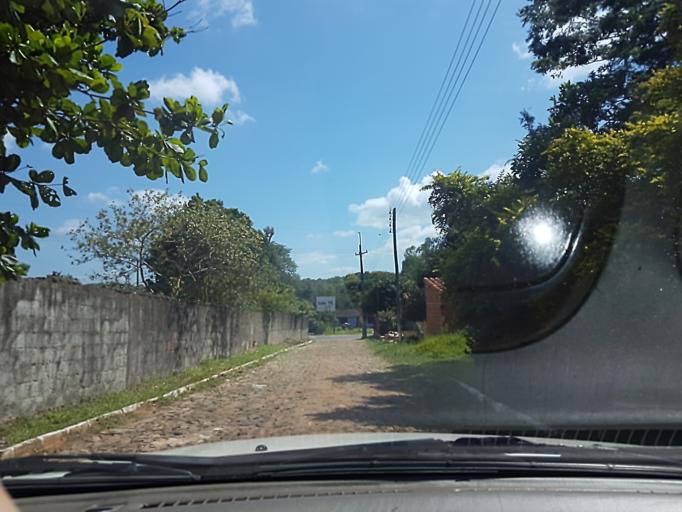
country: PY
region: Central
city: Limpio
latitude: -25.2365
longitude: -57.4439
